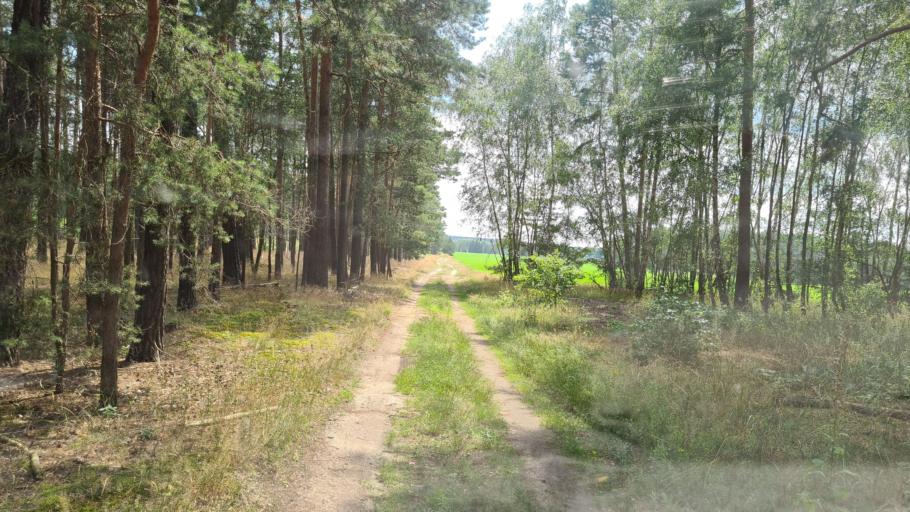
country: DE
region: Brandenburg
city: Bronkow
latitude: 51.7118
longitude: 13.8765
